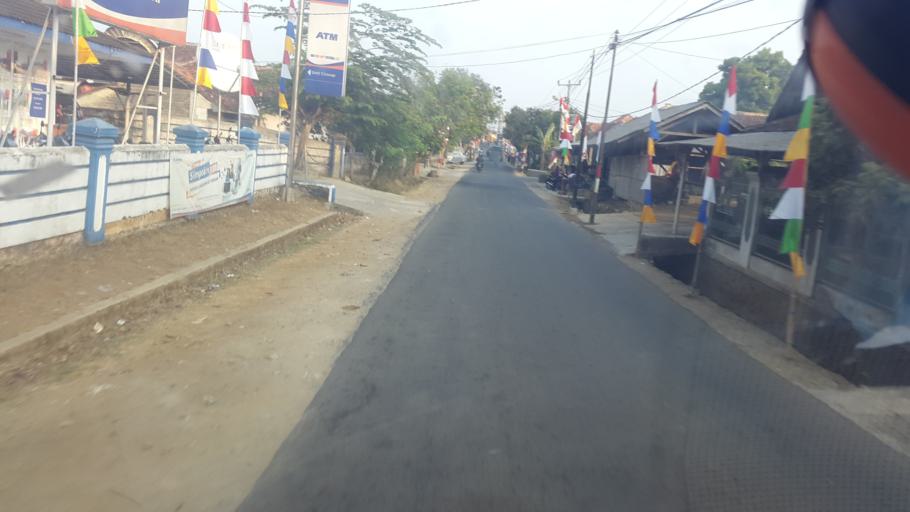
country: ID
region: West Java
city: Ciracap
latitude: -7.3319
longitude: 106.5220
